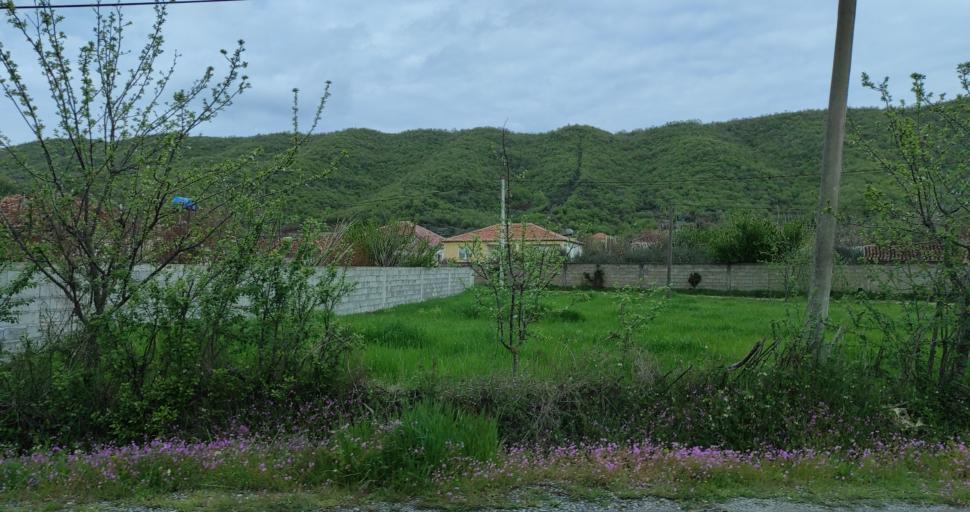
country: AL
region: Shkoder
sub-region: Rrethi i Shkodres
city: Dajc
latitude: 42.0206
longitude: 19.3809
